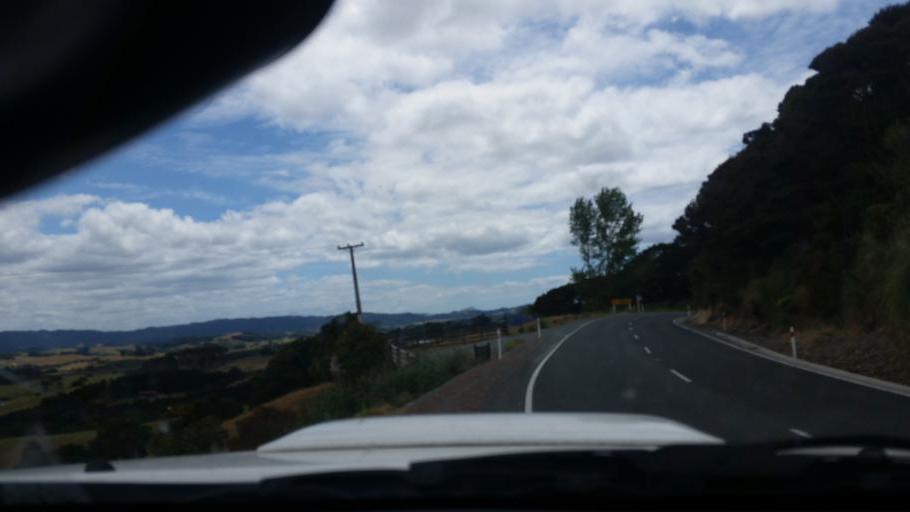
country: NZ
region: Auckland
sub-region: Auckland
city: Wellsford
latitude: -36.1629
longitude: 174.5824
